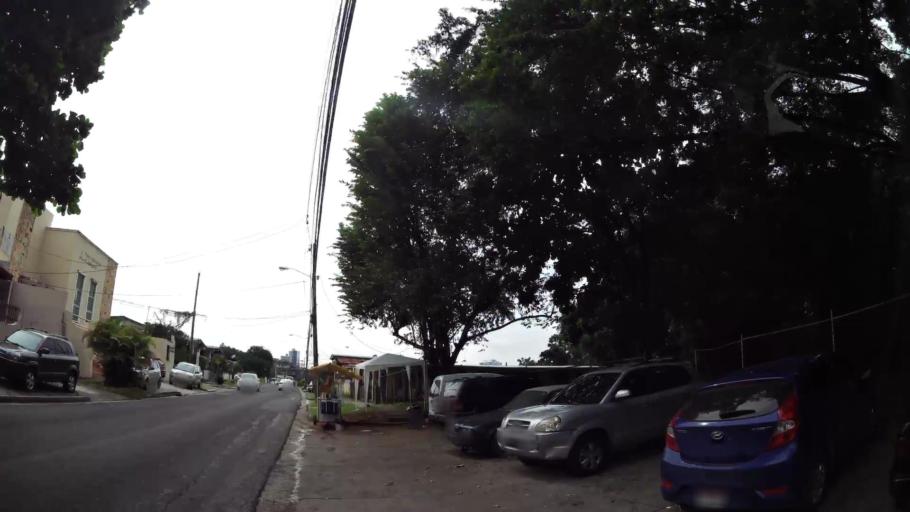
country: PA
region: Panama
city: Panama
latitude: 9.0195
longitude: -79.5204
